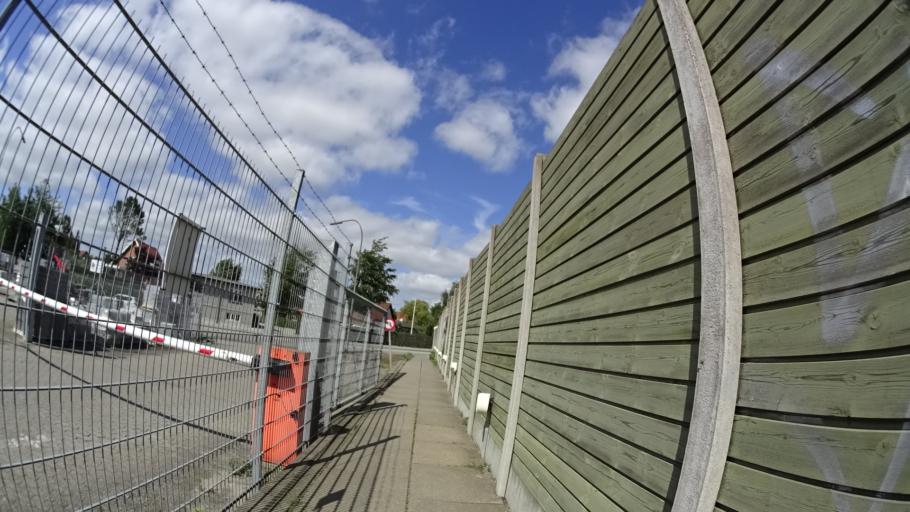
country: DK
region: Central Jutland
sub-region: Arhus Kommune
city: Stavtrup
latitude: 56.1464
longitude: 10.1541
